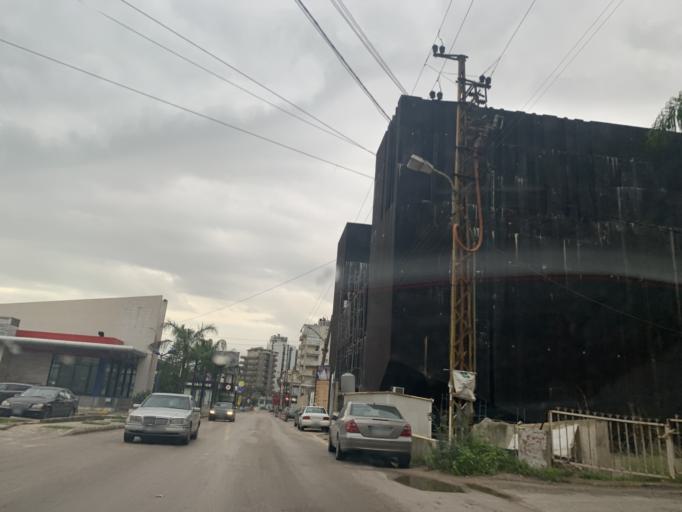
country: LB
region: Mont-Liban
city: Djounie
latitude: 33.9800
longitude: 35.6160
